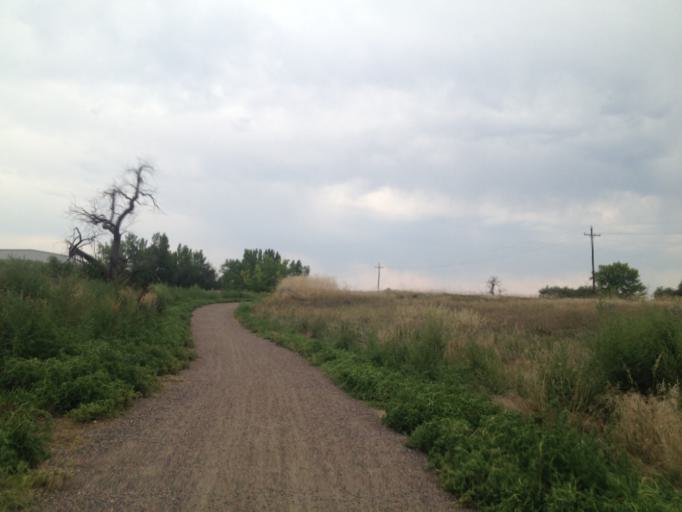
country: US
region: Colorado
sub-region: Boulder County
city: Lafayette
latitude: 40.0067
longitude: -105.0547
